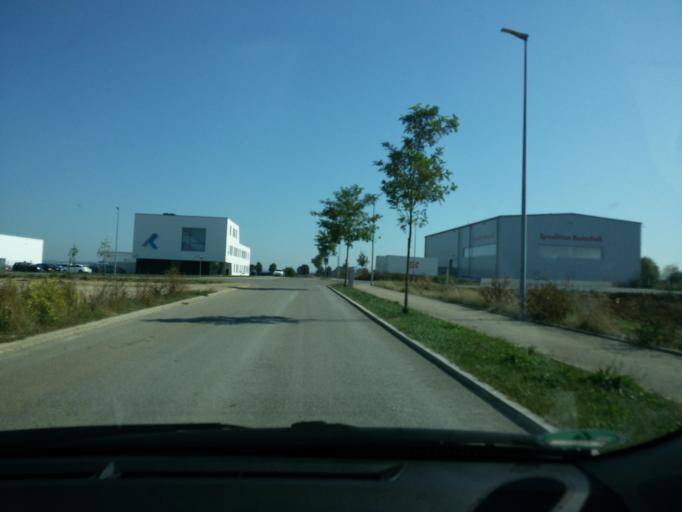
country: DE
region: Bavaria
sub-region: Swabia
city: Noerdlingen
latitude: 48.8618
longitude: 10.5192
